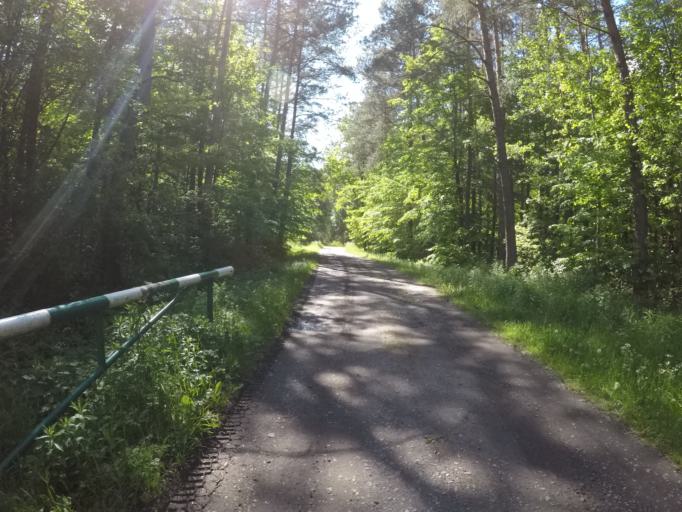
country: PL
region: Swietokrzyskie
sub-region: Powiat kielecki
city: Miedziana Gora
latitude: 50.9234
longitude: 20.5308
